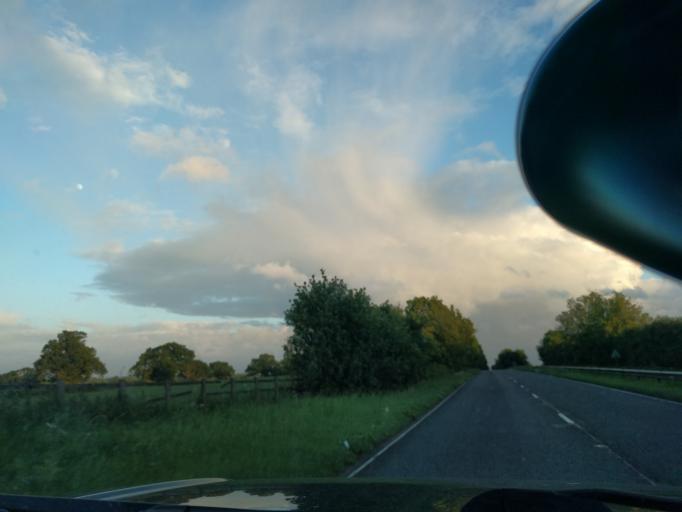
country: GB
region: England
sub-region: Wiltshire
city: Chippenham
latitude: 51.5090
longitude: -2.1248
